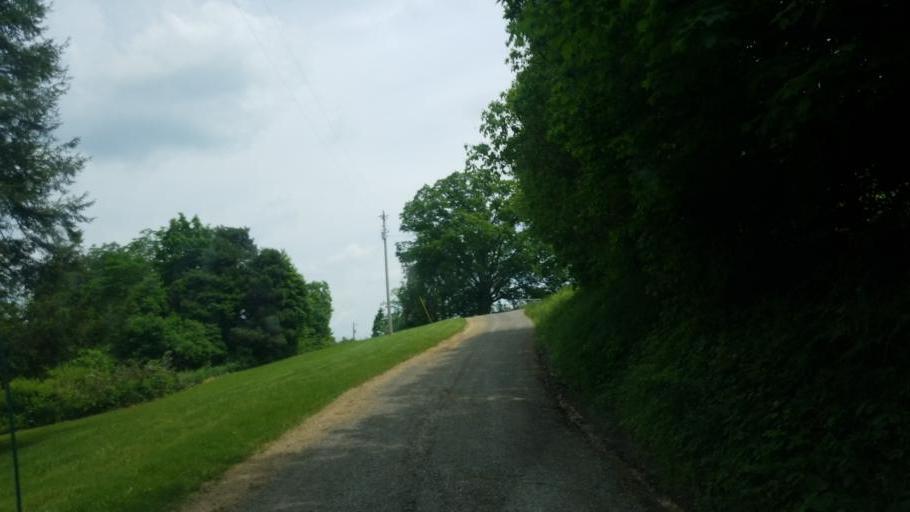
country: US
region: Ohio
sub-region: Holmes County
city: Millersburg
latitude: 40.4836
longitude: -81.8055
